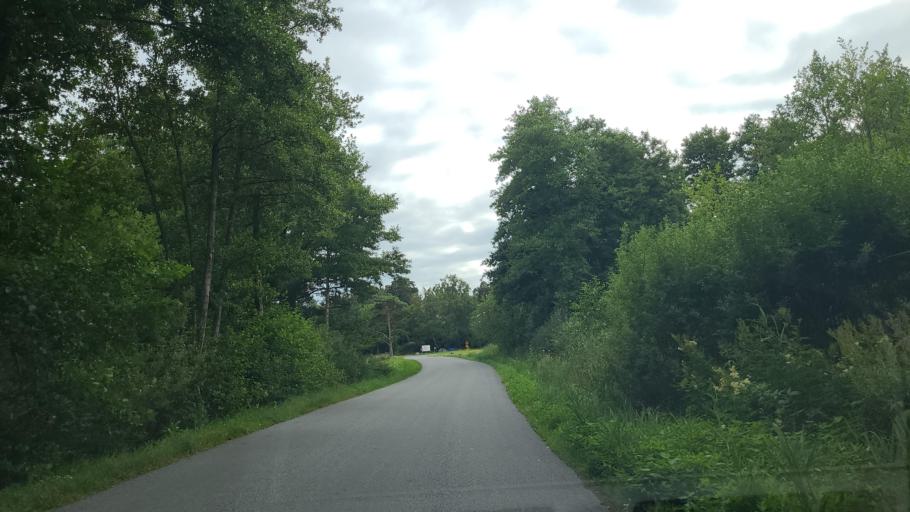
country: SE
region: Stockholm
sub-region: Upplands-Bro Kommun
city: Bro
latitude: 59.4771
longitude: 17.5615
